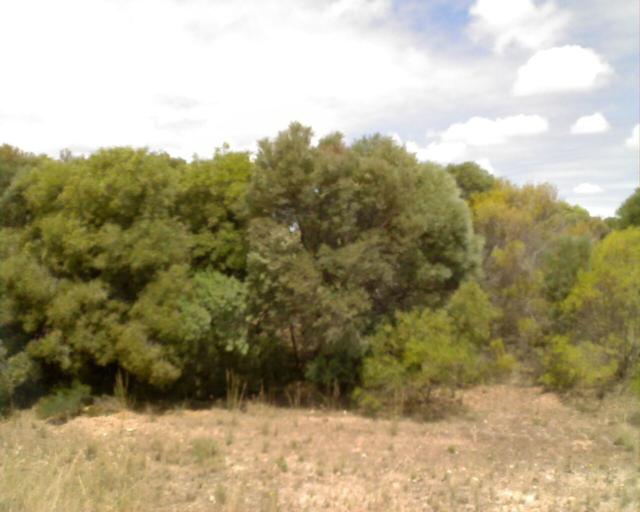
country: AU
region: South Australia
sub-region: Ceduna
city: Ceduna
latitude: -31.9317
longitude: 133.0125
